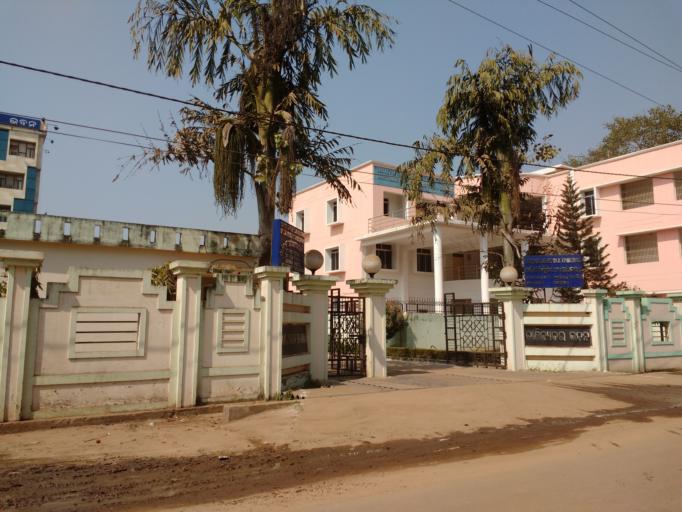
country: IN
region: Odisha
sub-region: Cuttack
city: Cuttack
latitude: 20.4810
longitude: 85.8718
